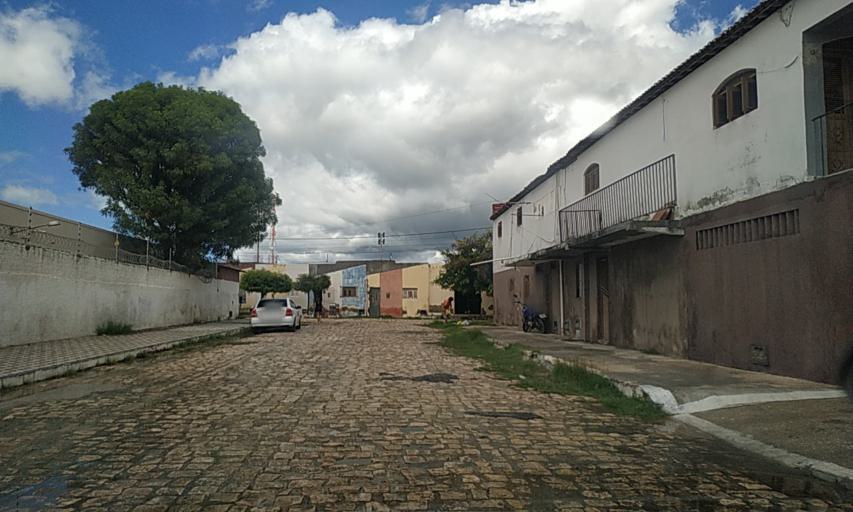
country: BR
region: Rio Grande do Norte
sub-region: Areia Branca
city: Areia Branca
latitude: -4.9525
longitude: -37.1302
